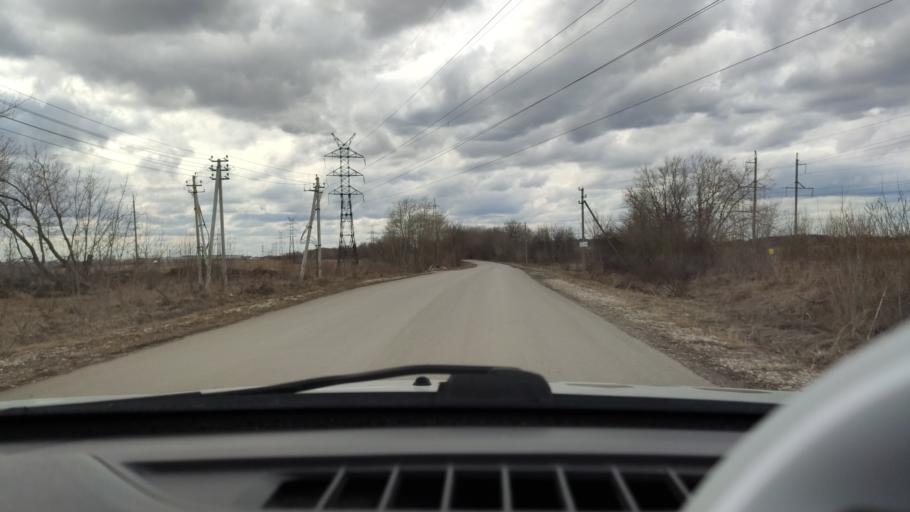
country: RU
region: Perm
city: Froly
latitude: 57.9286
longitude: 56.2594
